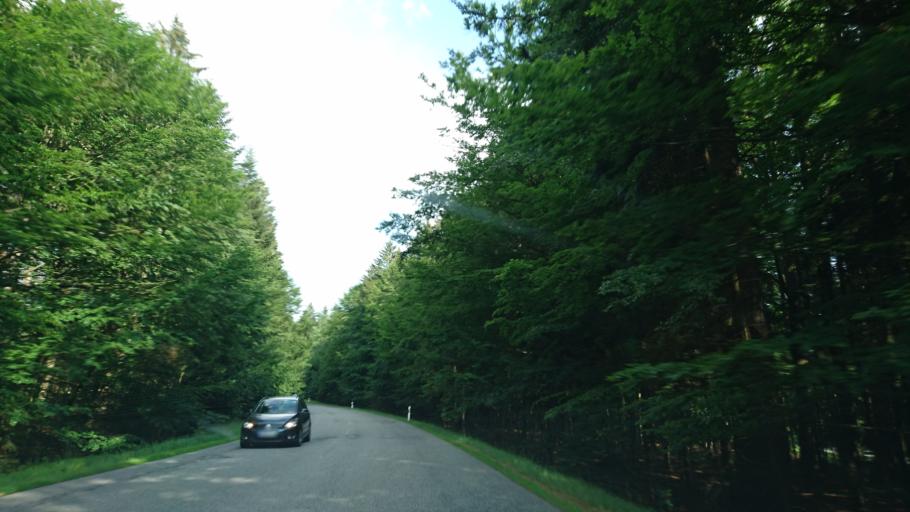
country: DE
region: Bavaria
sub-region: Lower Bavaria
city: Neuschonau
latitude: 48.8942
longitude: 13.4783
